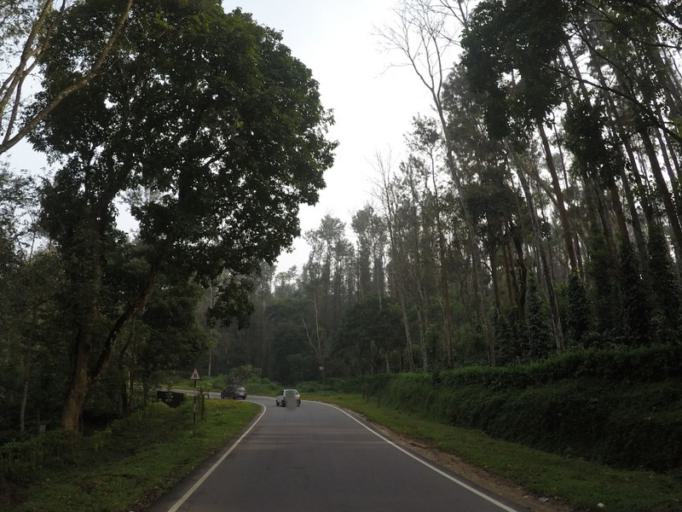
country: IN
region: Karnataka
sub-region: Chikmagalur
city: Mudigere
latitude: 13.2598
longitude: 75.6310
